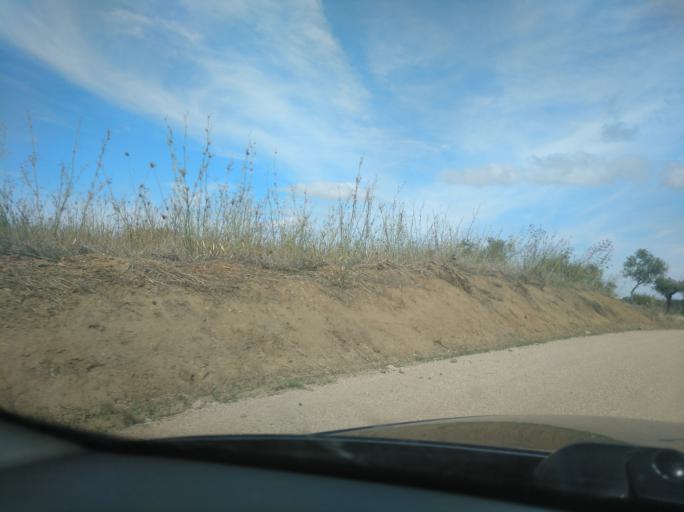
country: PT
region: Portalegre
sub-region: Campo Maior
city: Campo Maior
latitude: 39.0389
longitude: -7.0591
